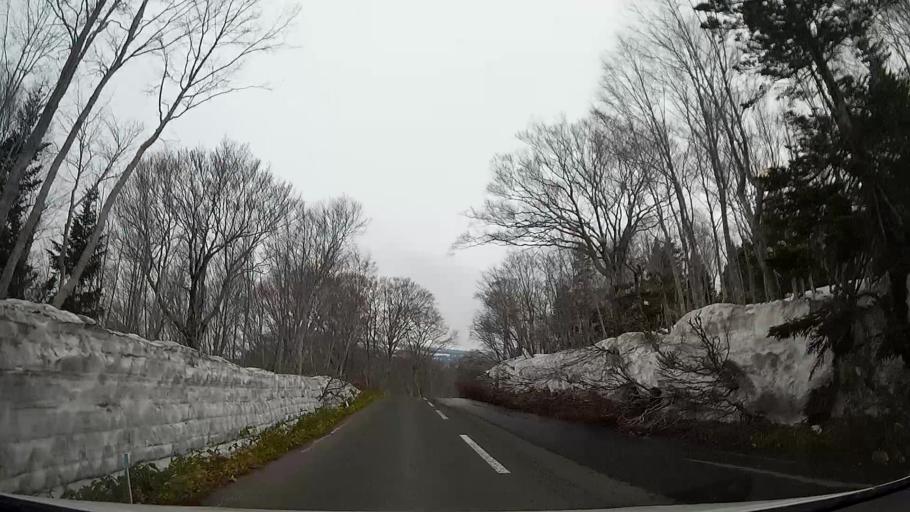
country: JP
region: Aomori
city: Aomori Shi
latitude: 40.6316
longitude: 140.9049
